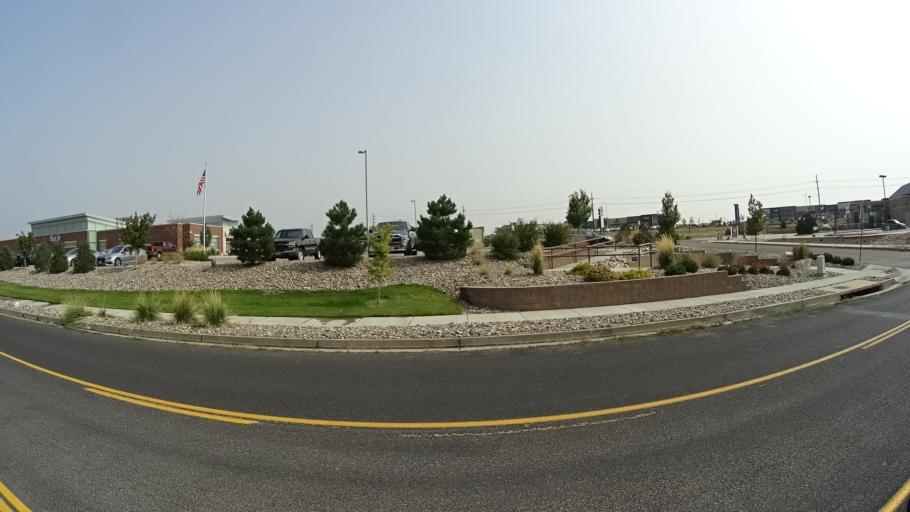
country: US
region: Colorado
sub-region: El Paso County
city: Cimarron Hills
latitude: 38.9238
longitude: -104.7214
